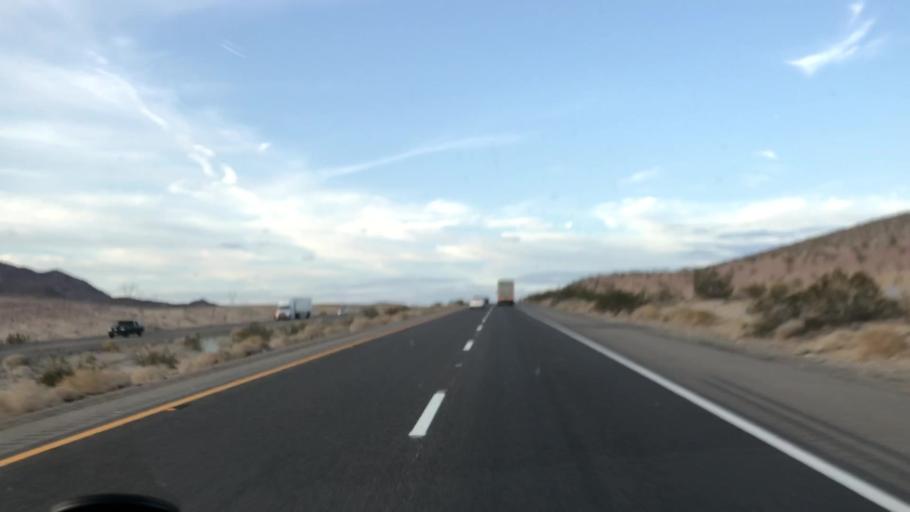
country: US
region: California
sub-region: San Bernardino County
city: Fort Irwin
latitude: 35.1171
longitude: -116.2369
